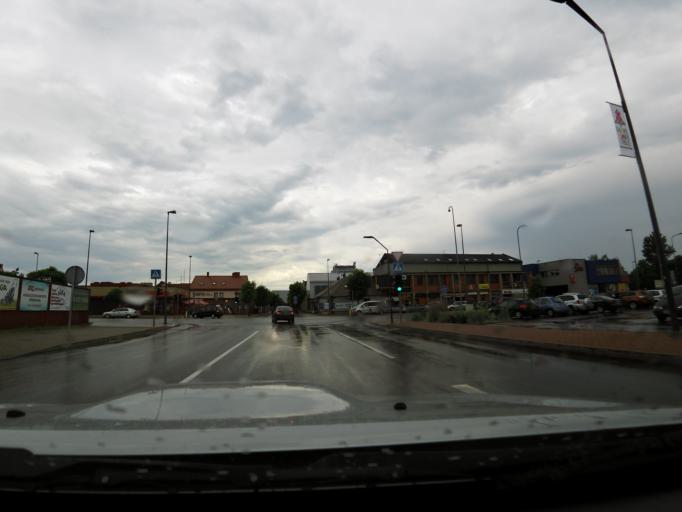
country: LT
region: Marijampoles apskritis
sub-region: Marijampole Municipality
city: Marijampole
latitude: 54.5562
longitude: 23.3552
